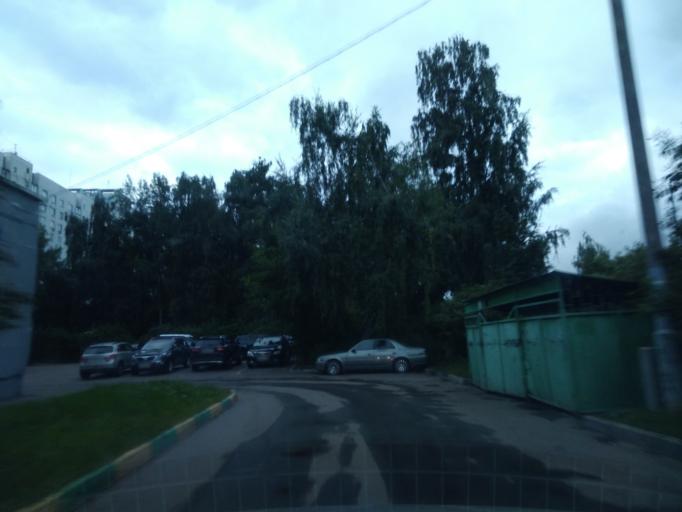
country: RU
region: Moscow
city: Strogino
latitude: 55.8056
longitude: 37.4029
